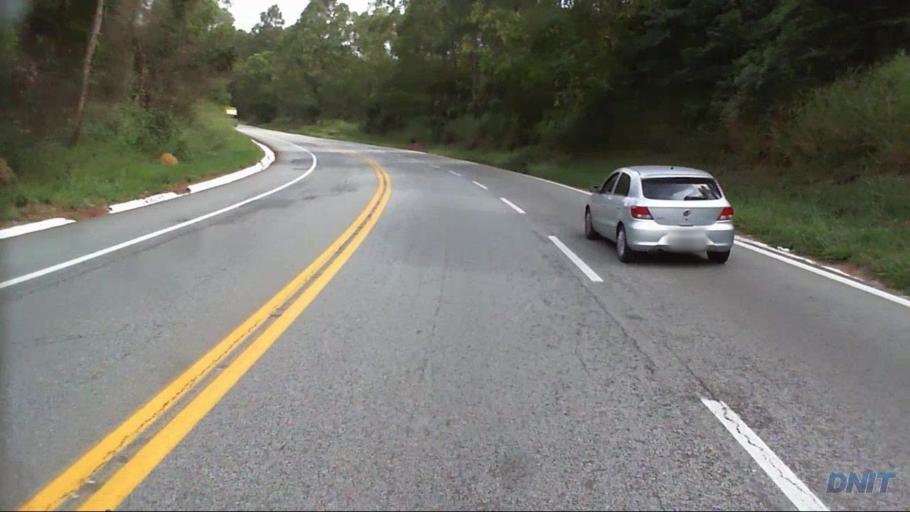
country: BR
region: Minas Gerais
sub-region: Caete
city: Caete
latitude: -19.7269
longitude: -43.5926
